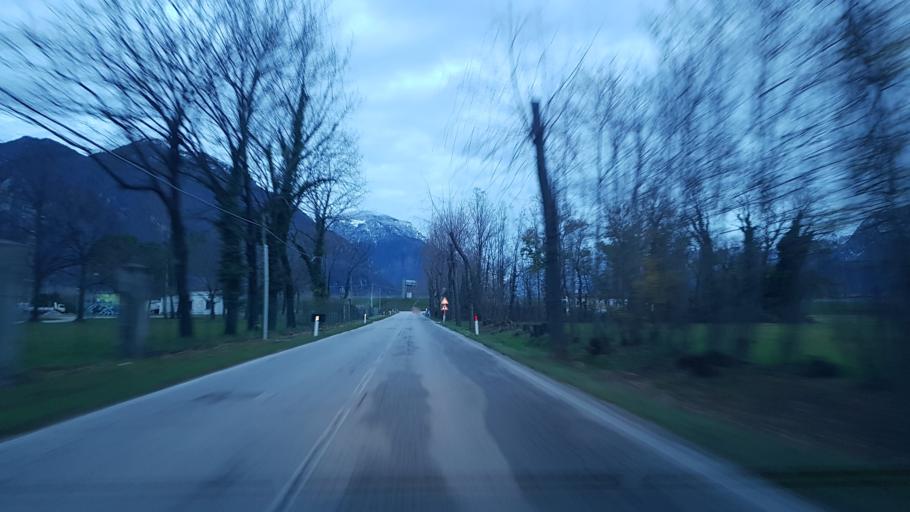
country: IT
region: Friuli Venezia Giulia
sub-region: Provincia di Udine
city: Osoppo
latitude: 46.2640
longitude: 13.0890
